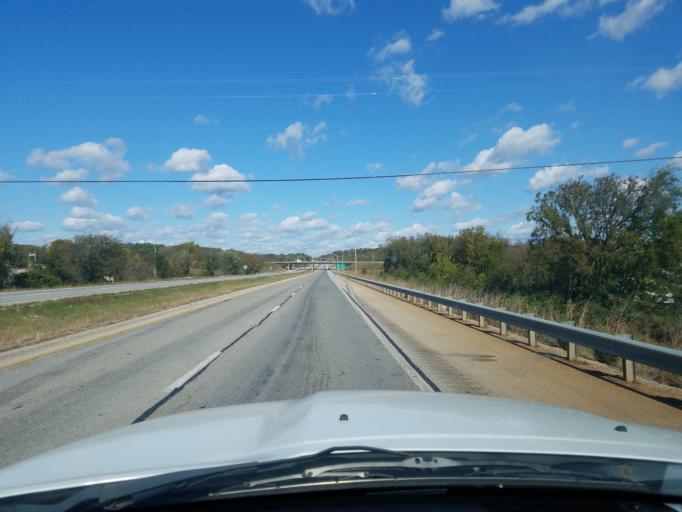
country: US
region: Kentucky
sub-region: Warren County
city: Bowling Green
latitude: 36.9881
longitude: -86.5029
